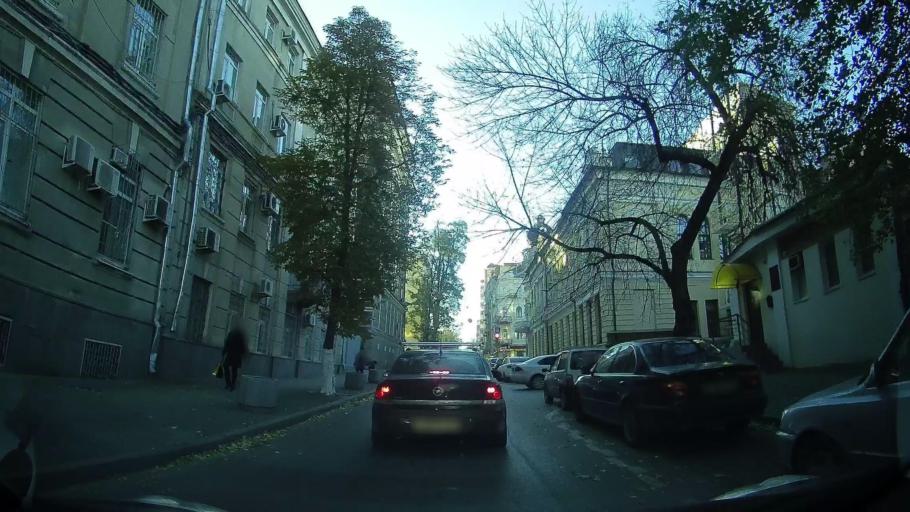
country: RU
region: Rostov
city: Rostov-na-Donu
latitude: 47.2197
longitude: 39.7023
